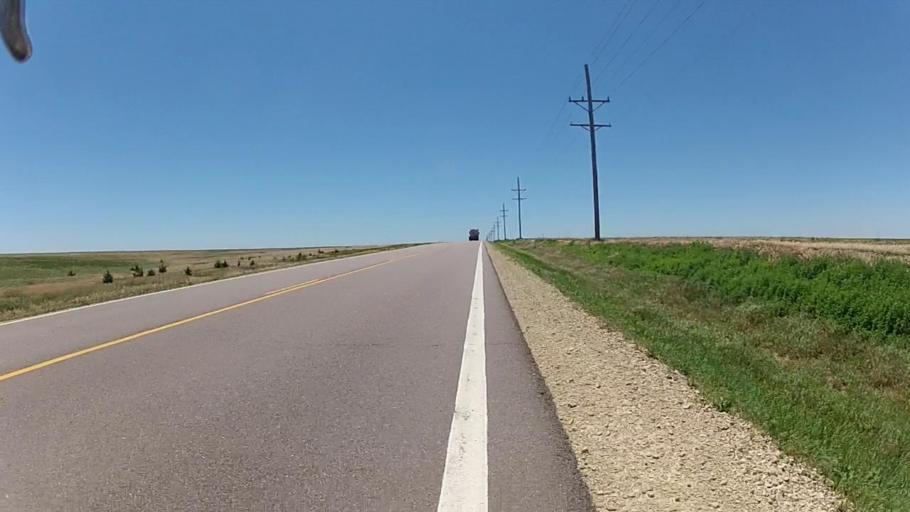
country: US
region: Kansas
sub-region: Kiowa County
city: Greensburg
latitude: 37.5388
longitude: -99.3210
